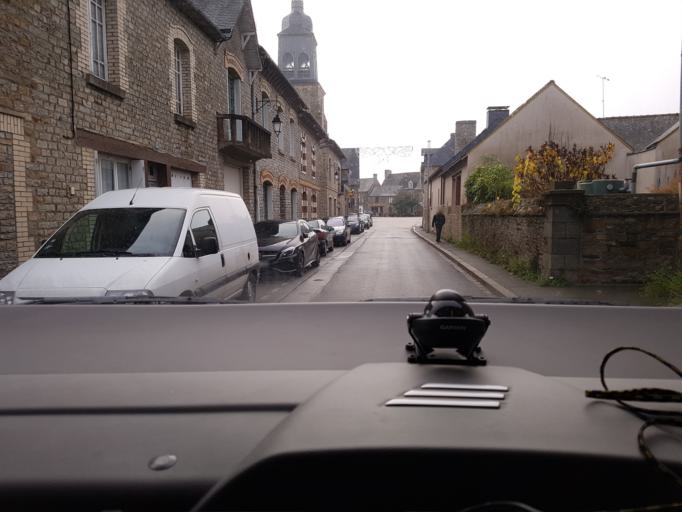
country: FR
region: Brittany
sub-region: Departement d'Ille-et-Vilaine
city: Livre-sur-Changeon
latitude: 48.1779
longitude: -1.3024
